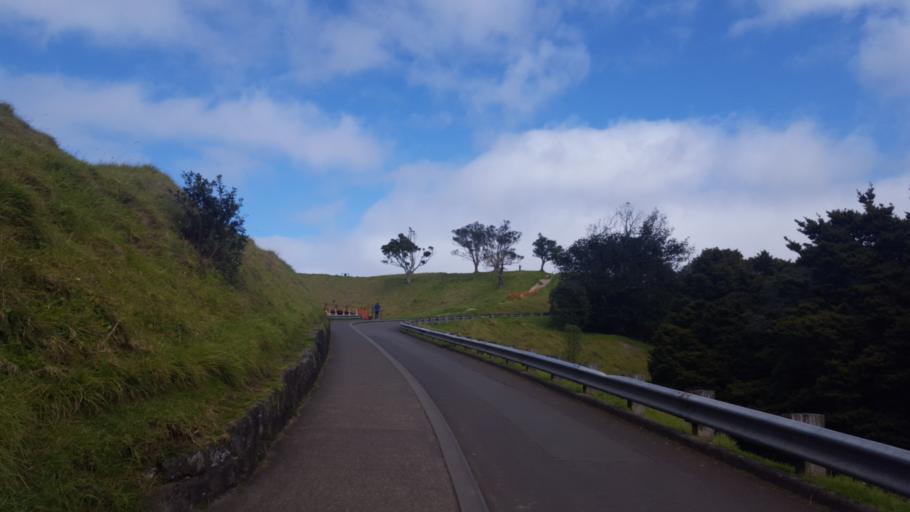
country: NZ
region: Auckland
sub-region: Auckland
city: Auckland
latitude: -36.8761
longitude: 174.7642
